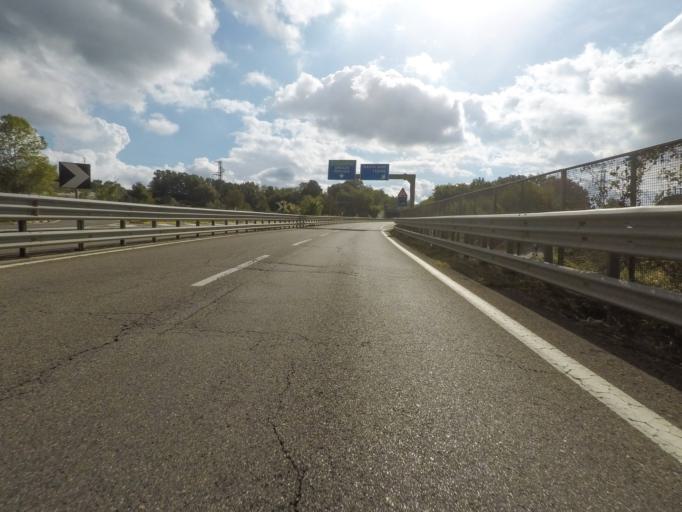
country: IT
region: Tuscany
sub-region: Provincia di Siena
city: Rapolano Terme
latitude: 43.3025
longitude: 11.5968
